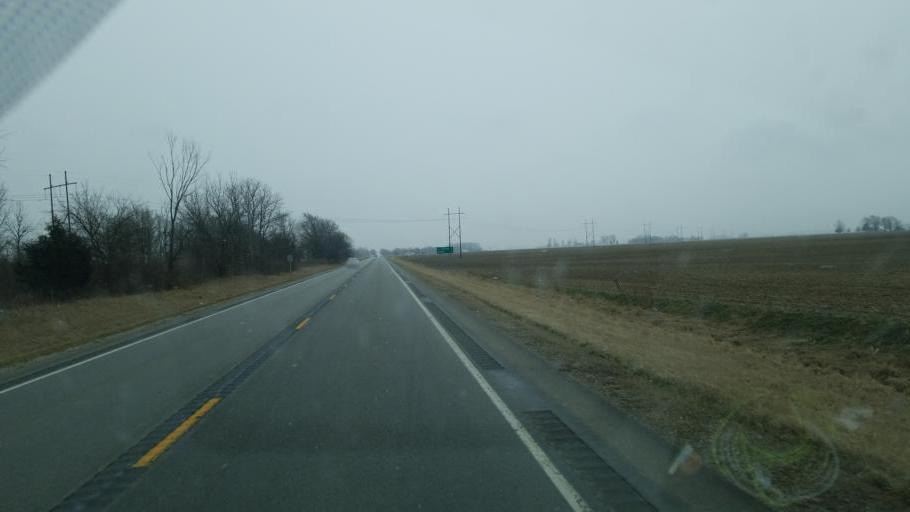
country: US
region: Indiana
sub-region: Wabash County
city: Wabash
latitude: 40.7633
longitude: -85.8153
